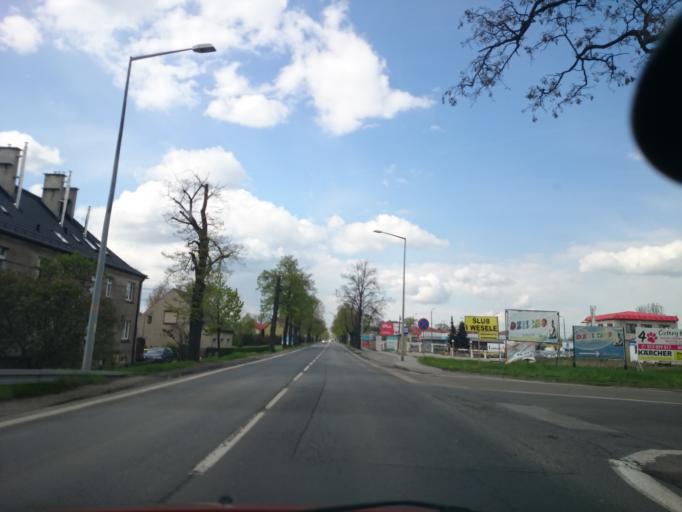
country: PL
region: Opole Voivodeship
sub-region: Powiat opolski
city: Opole
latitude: 50.6529
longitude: 17.9617
